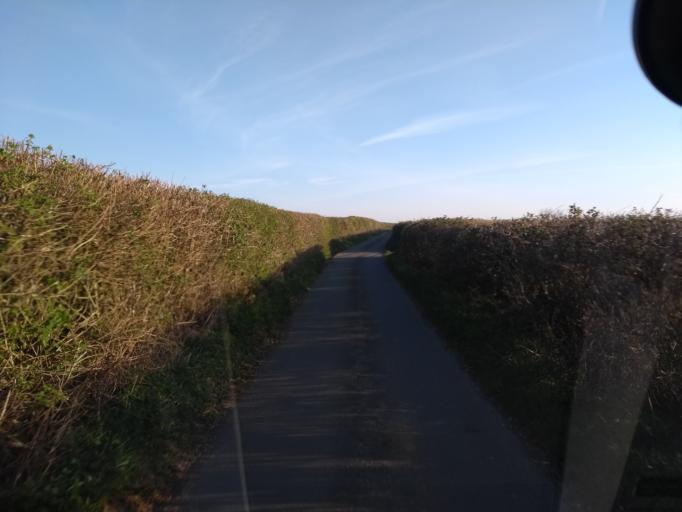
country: GB
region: England
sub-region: Somerset
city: Crewkerne
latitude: 50.8562
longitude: -2.8139
